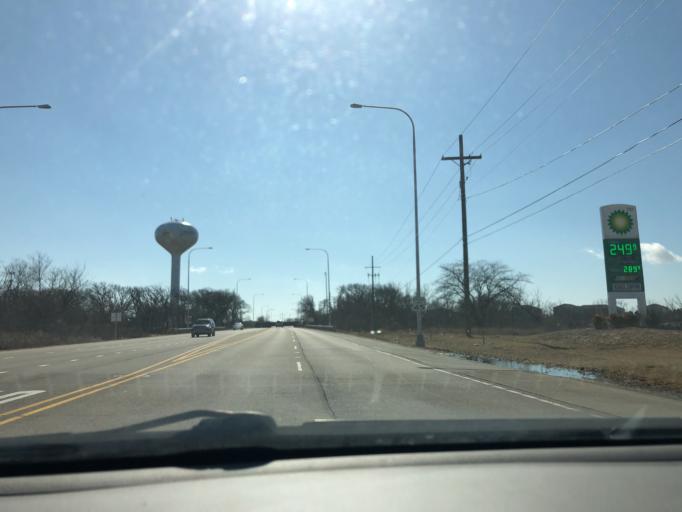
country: US
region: Illinois
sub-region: Kane County
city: Pingree Grove
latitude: 42.0879
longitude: -88.4567
